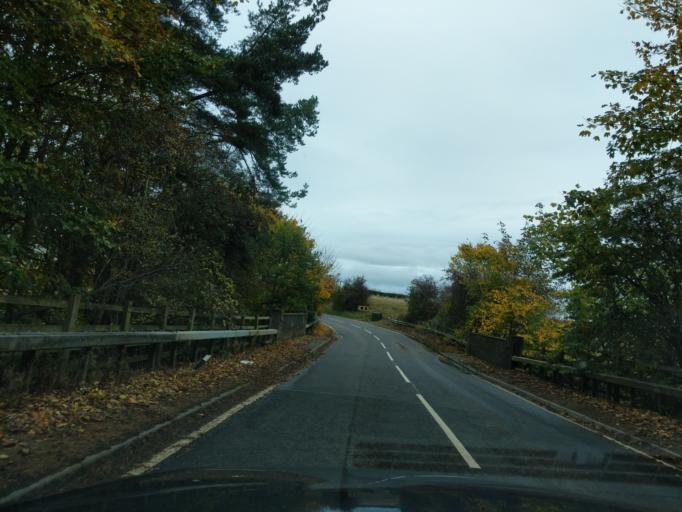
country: GB
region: Scotland
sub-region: Fife
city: Saint Andrews
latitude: 56.2949
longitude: -2.7526
